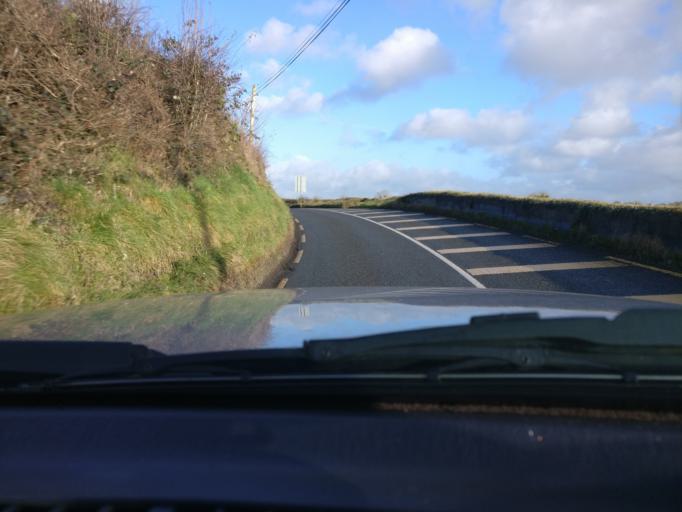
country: IE
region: Leinster
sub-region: Uibh Fhaili
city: Clara
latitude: 53.3998
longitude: -7.5797
